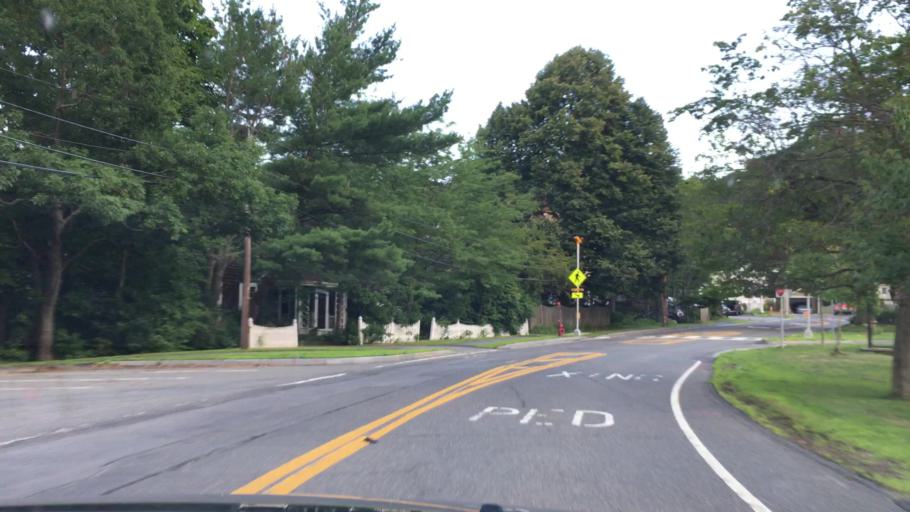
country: US
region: Massachusetts
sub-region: Essex County
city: Essex
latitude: 42.5797
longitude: -70.7629
